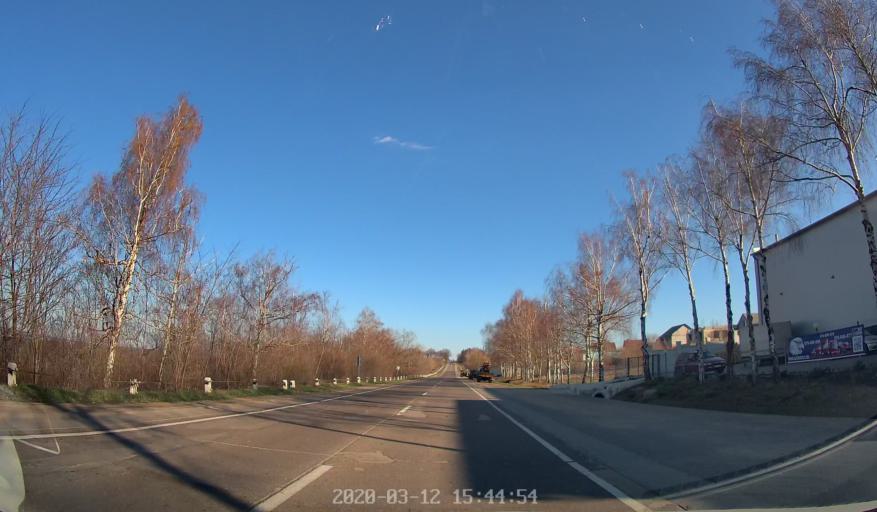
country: MD
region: Chisinau
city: Stauceni
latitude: 47.1089
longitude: 28.8673
